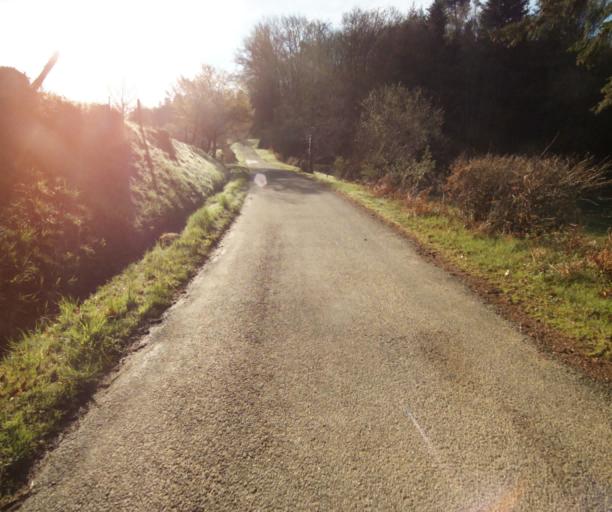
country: FR
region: Limousin
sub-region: Departement de la Correze
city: Laguenne
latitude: 45.2791
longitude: 1.8581
